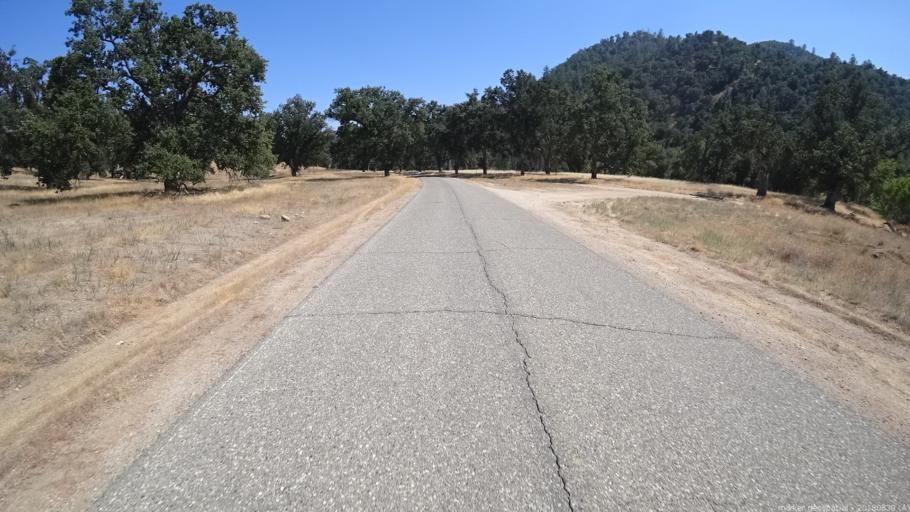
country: US
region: California
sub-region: Monterey County
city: Greenfield
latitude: 36.0728
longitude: -121.3648
